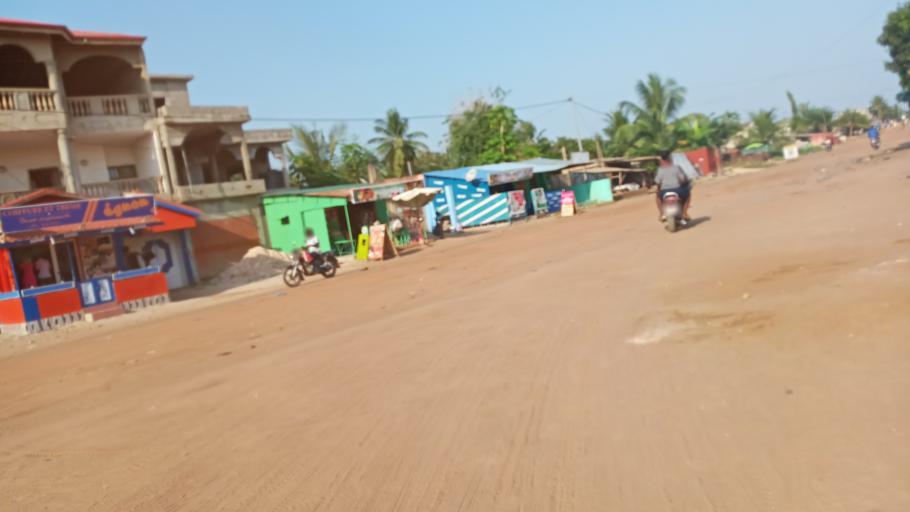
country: TG
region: Maritime
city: Lome
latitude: 6.1792
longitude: 1.1506
